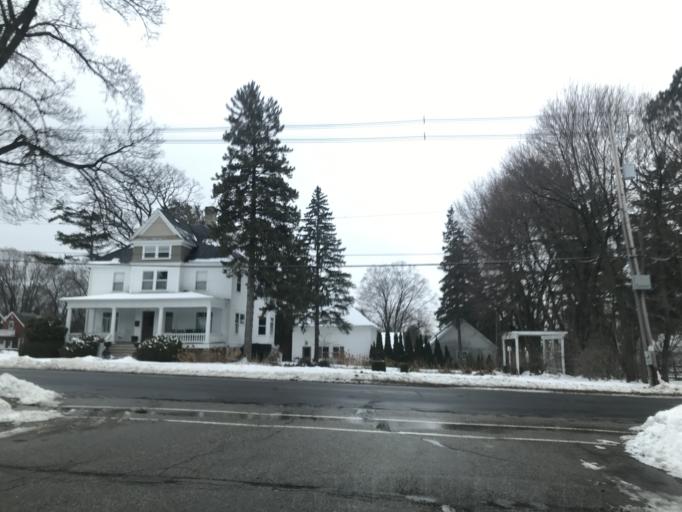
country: US
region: Wisconsin
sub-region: Door County
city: Sturgeon Bay
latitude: 44.8354
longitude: -87.3710
